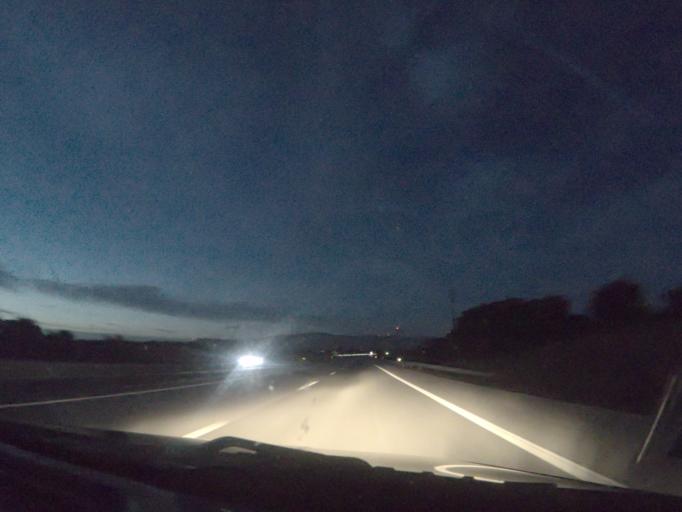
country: PT
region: Guarda
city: Alcains
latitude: 39.9618
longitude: -7.4567
